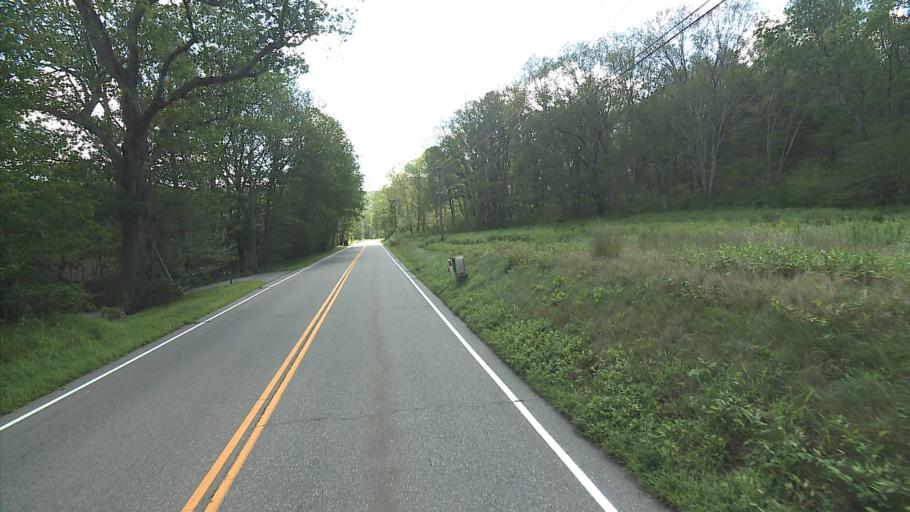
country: US
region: Connecticut
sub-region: Windham County
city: South Woodstock
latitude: 41.8626
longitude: -72.0929
